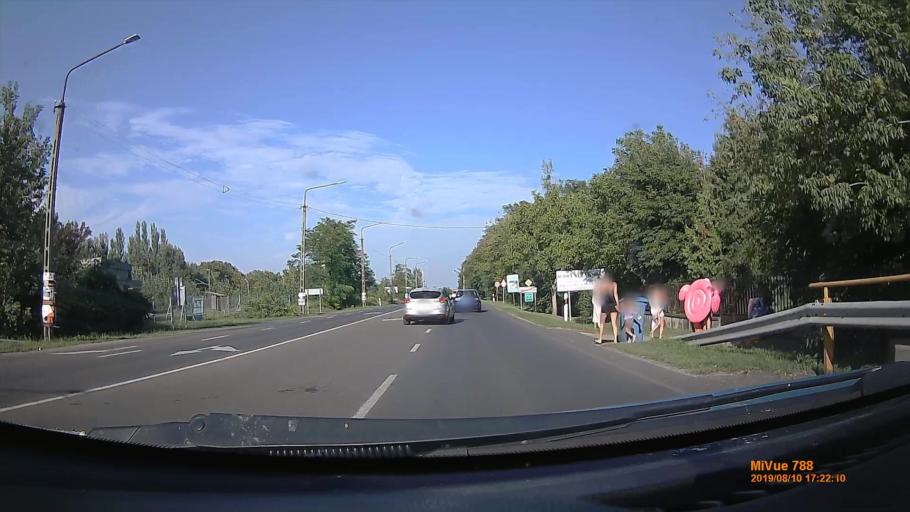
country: HU
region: Somogy
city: Balatonlelle
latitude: 46.7957
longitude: 17.7262
